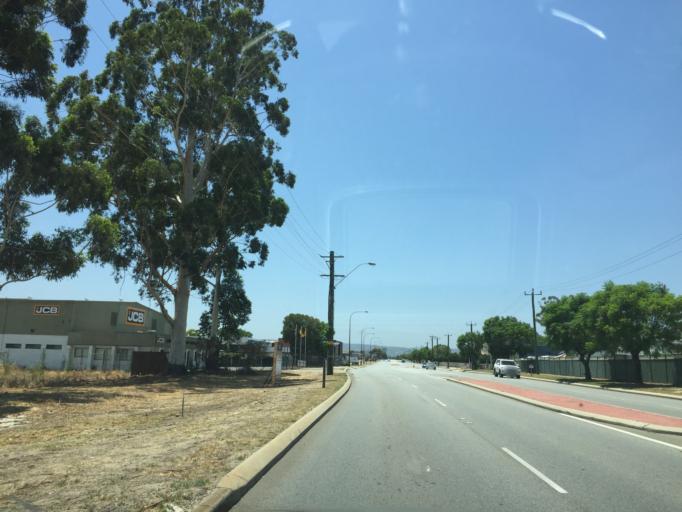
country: AU
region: Western Australia
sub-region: Canning
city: Queens Park
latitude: -31.9967
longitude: 115.9452
